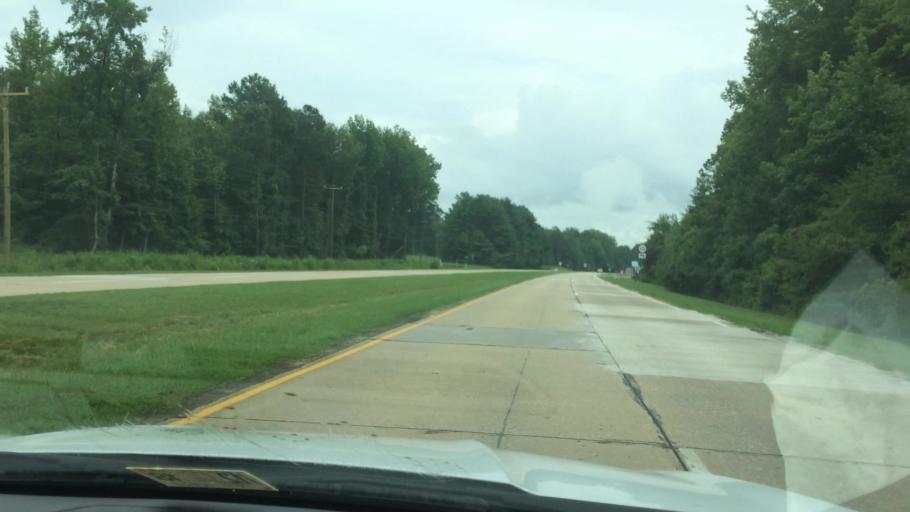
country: US
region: Virginia
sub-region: New Kent County
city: New Kent
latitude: 37.4420
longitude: -77.0395
